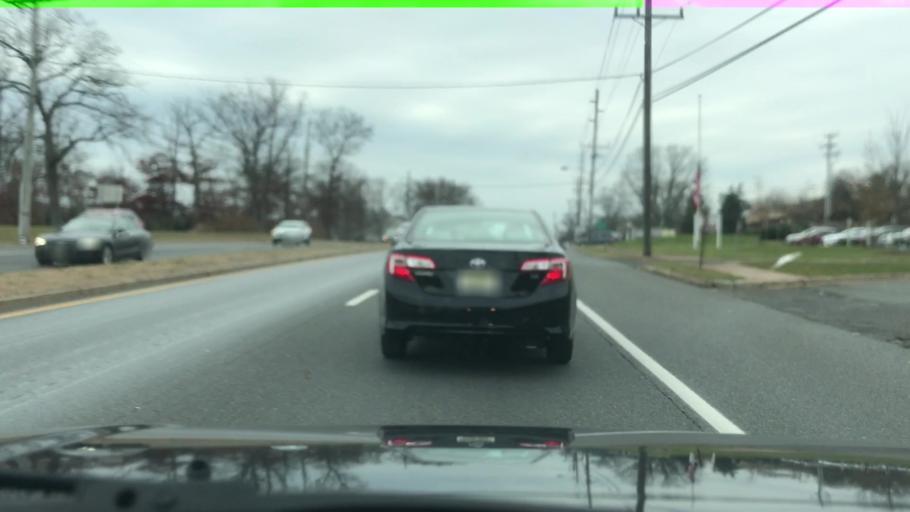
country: US
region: New Jersey
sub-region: Ocean County
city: Toms River
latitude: 39.9762
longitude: -74.1832
